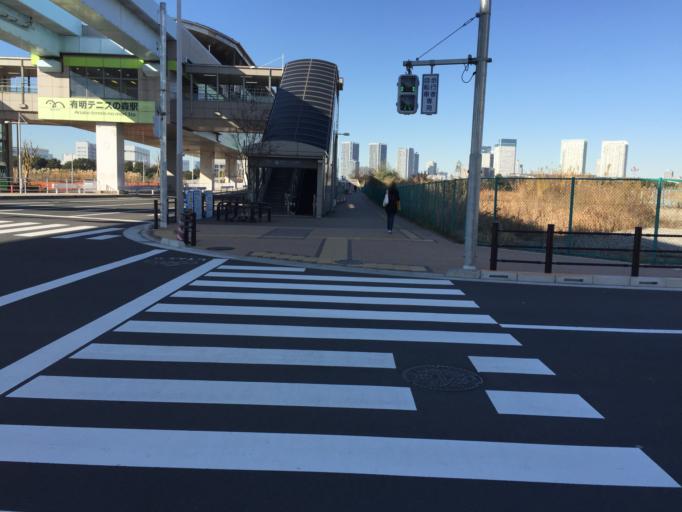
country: JP
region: Tokyo
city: Urayasu
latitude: 35.6395
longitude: 139.7897
